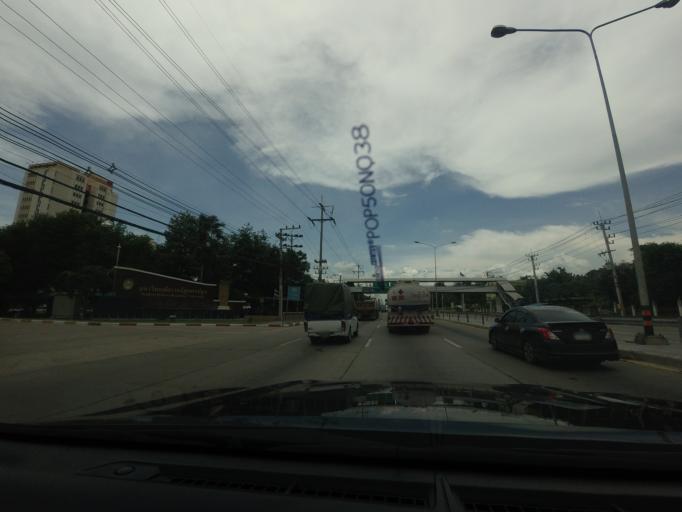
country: TH
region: Nakhon Pathom
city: Nakhon Pathom
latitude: 13.8378
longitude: 100.0304
